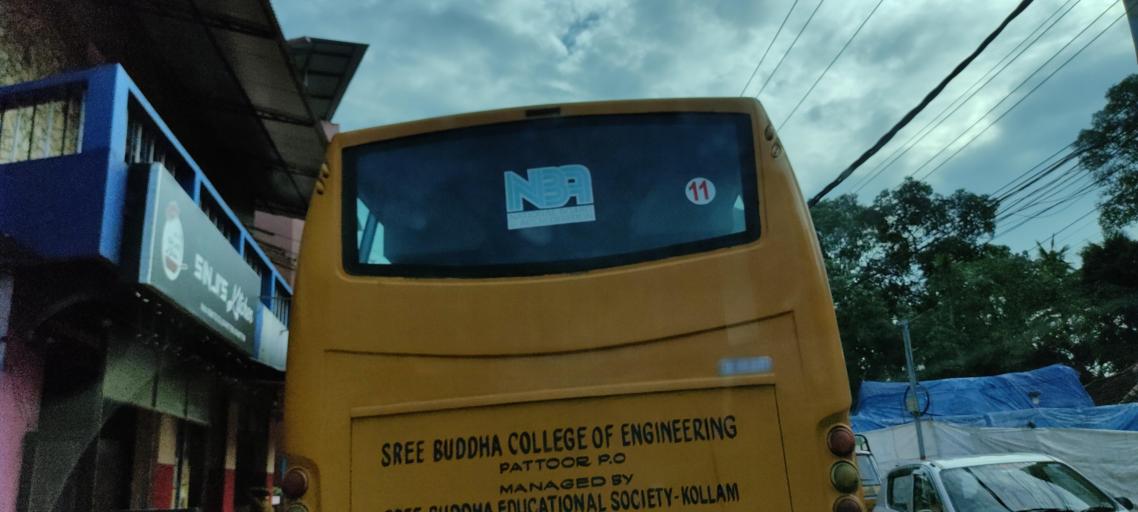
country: IN
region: Kerala
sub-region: Alappuzha
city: Mavelikara
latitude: 9.2536
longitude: 76.5470
